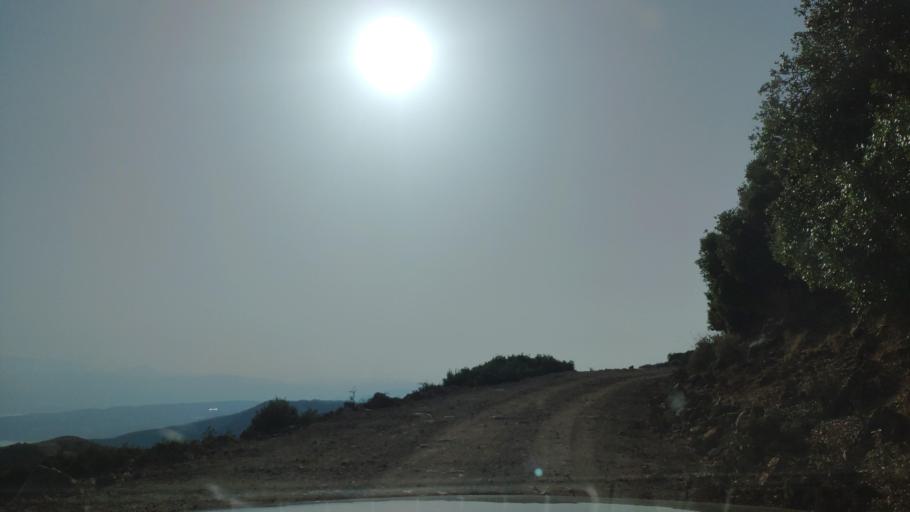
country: GR
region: West Greece
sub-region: Nomos Aitolias kai Akarnanias
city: Monastirakion
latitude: 38.8370
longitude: 20.9801
